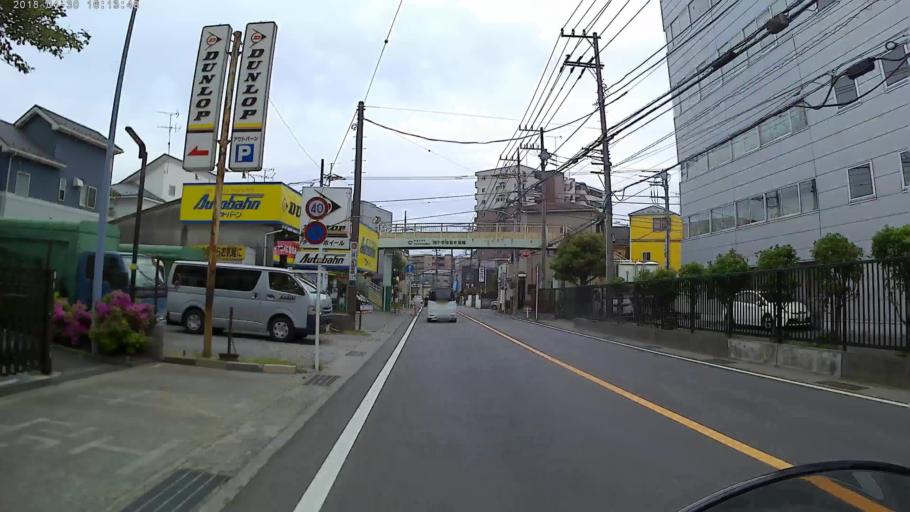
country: JP
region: Kanagawa
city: Minami-rinkan
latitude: 35.4886
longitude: 139.4311
